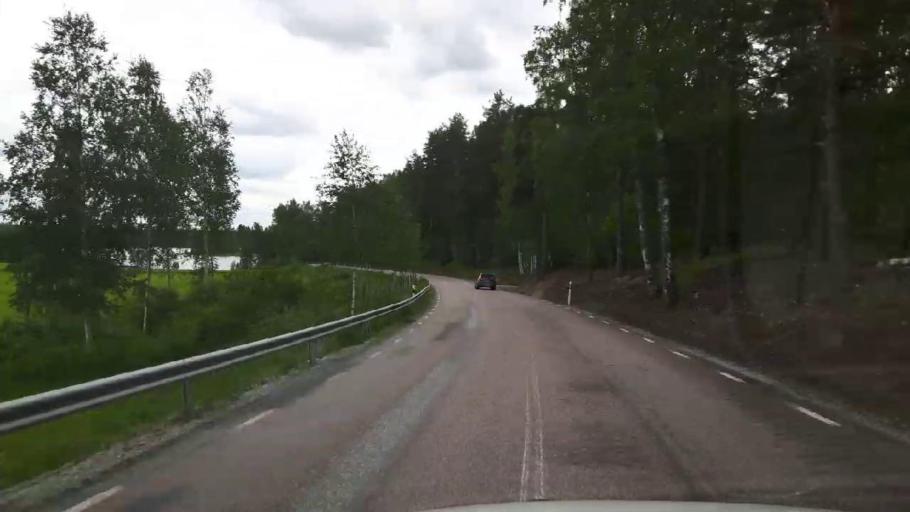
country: SE
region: Vaestmanland
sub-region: Skinnskattebergs Kommun
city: Skinnskatteberg
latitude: 59.8561
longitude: 15.8416
